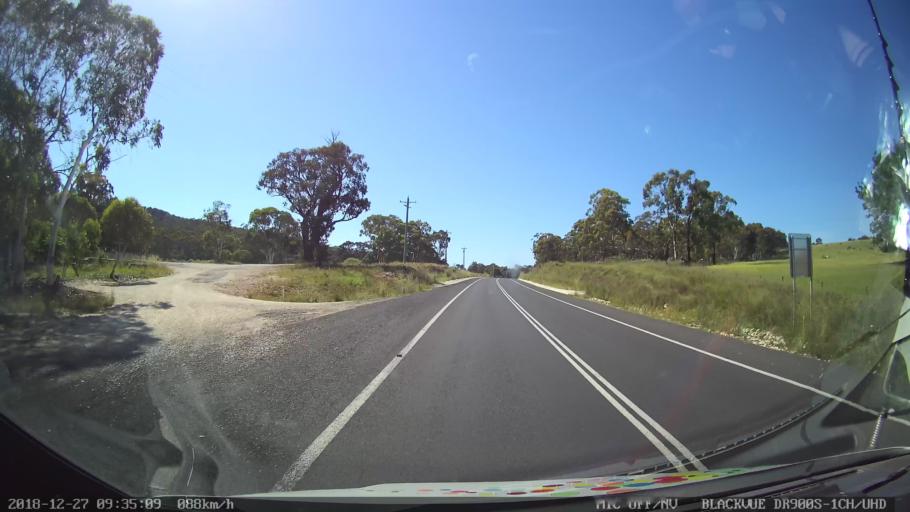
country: AU
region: New South Wales
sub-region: Lithgow
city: Portland
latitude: -33.2350
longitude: 150.0281
